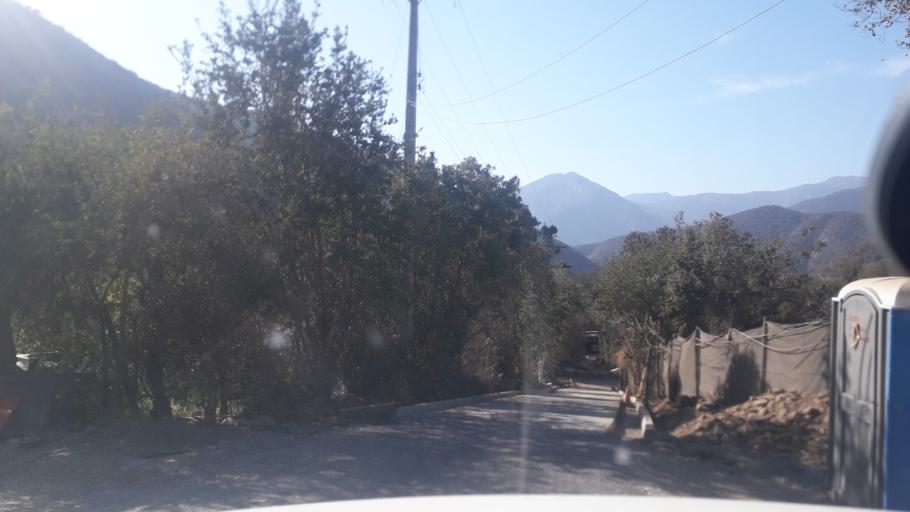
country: CL
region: Valparaiso
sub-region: Provincia de Marga Marga
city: Limache
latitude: -33.0785
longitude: -71.1003
